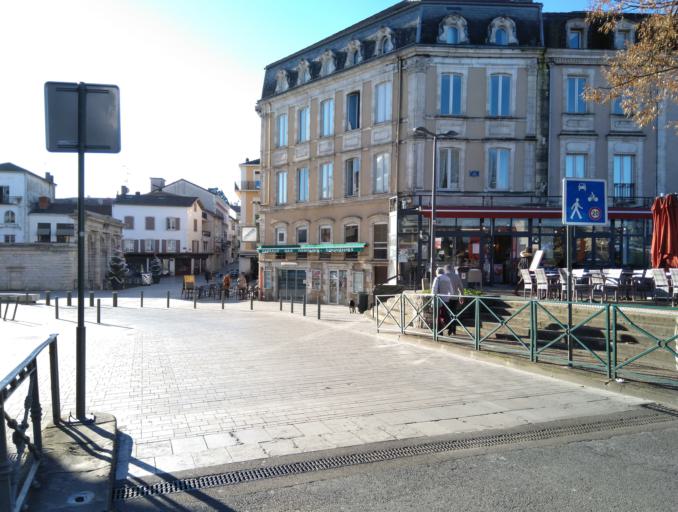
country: FR
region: Aquitaine
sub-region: Departement des Landes
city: Dax
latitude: 43.7115
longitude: -1.0532
